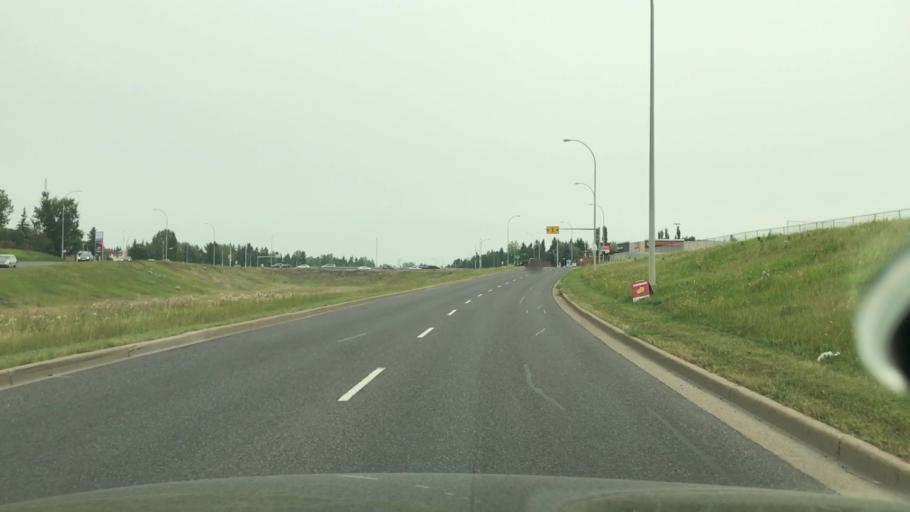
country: CA
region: Alberta
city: Edmonton
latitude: 53.4742
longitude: -113.5766
